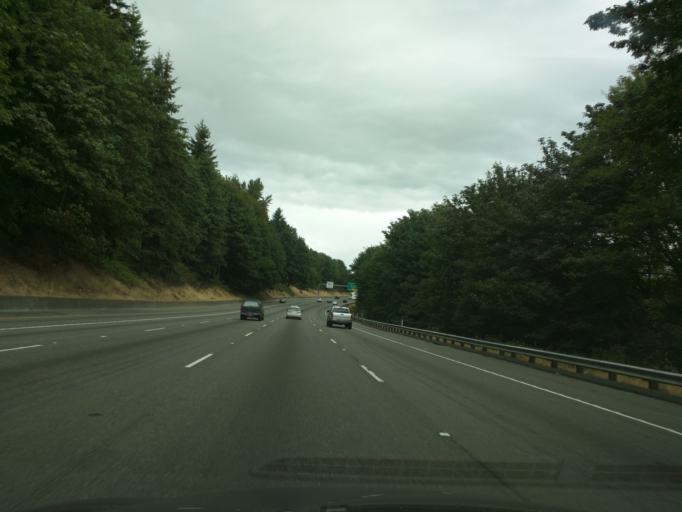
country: US
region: Washington
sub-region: Snohomish County
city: Everett
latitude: 47.9378
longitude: -122.1965
